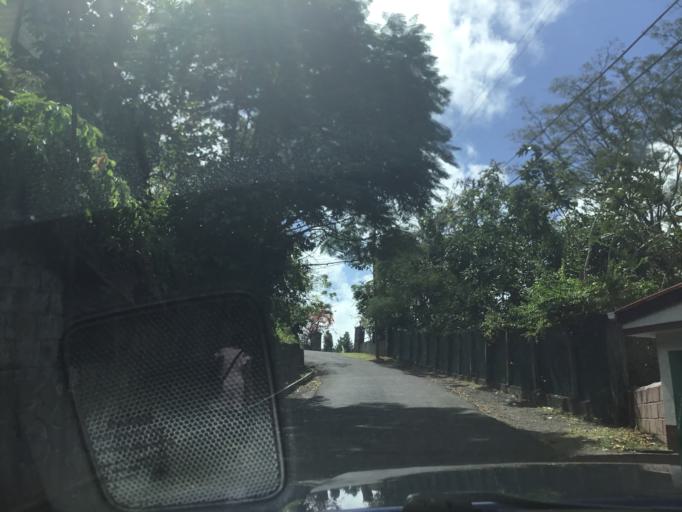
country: VC
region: Saint George
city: Kingstown Park
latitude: 13.1584
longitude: -61.2342
